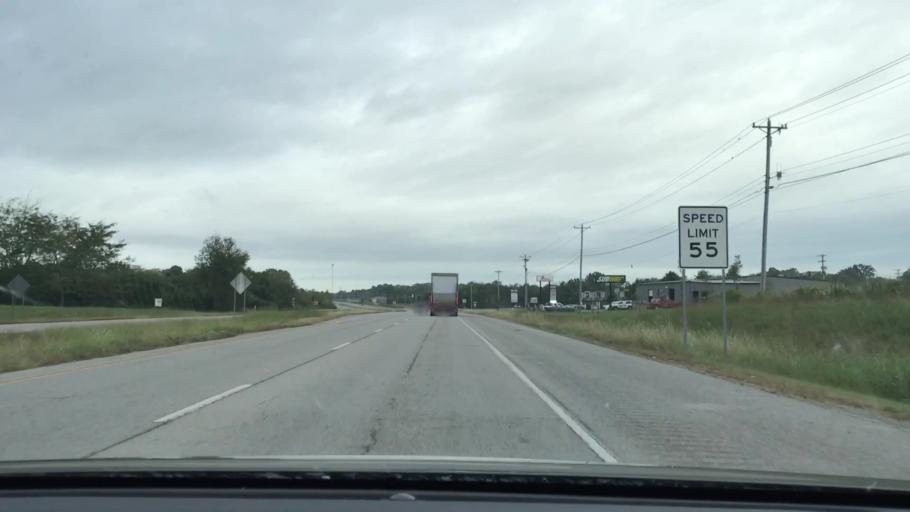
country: US
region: Kentucky
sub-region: Christian County
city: Hopkinsville
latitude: 36.8229
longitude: -87.5062
